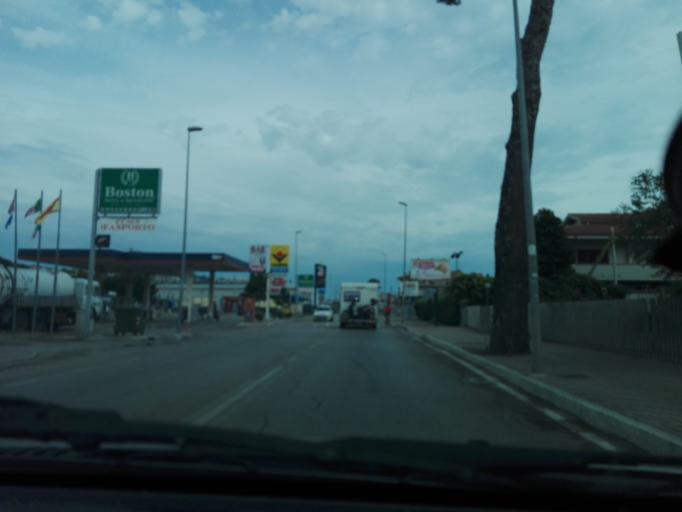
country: IT
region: Abruzzo
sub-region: Provincia di Teramo
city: Silvi
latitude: 42.5379
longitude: 14.1267
